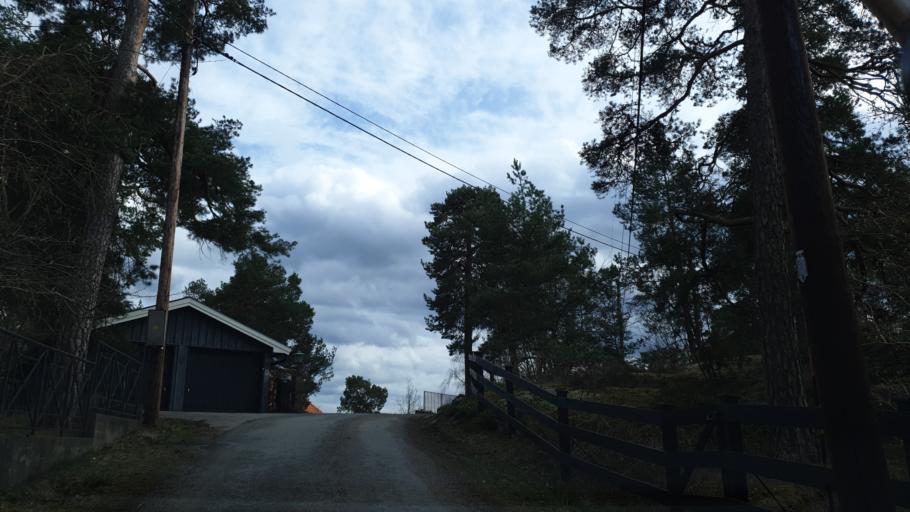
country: SE
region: Stockholm
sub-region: Nacka Kommun
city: Saltsjobaden
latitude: 59.2682
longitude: 18.3124
